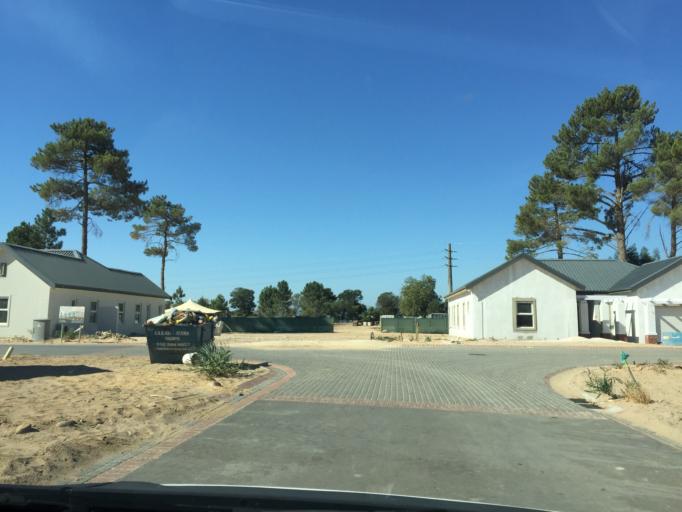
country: ZA
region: Western Cape
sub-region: Cape Winelands District Municipality
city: Paarl
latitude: -33.8067
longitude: 18.9662
